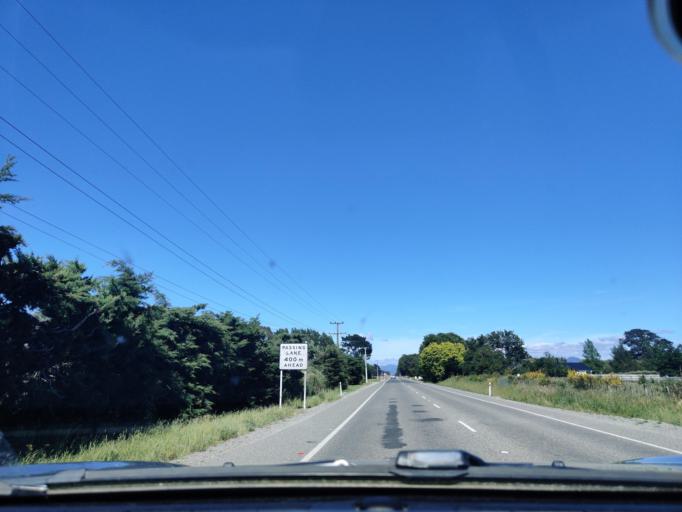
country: NZ
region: Wellington
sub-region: Masterton District
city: Masterton
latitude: -41.0923
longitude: 175.4444
